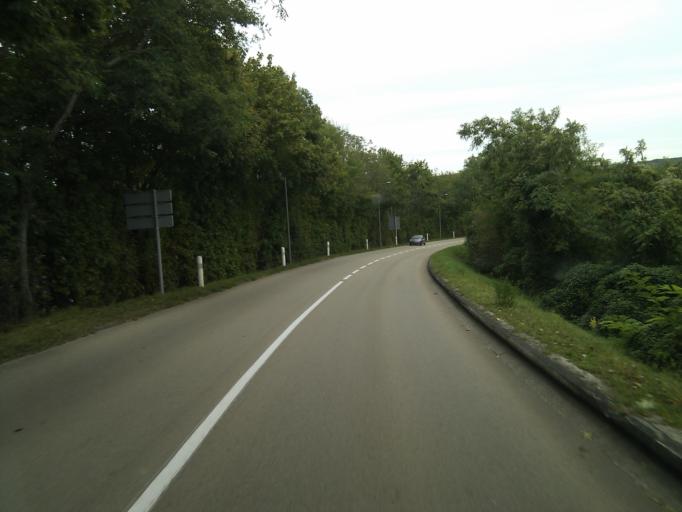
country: FR
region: Champagne-Ardenne
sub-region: Departement de la Haute-Marne
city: Chaumont
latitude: 48.1223
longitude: 5.1462
